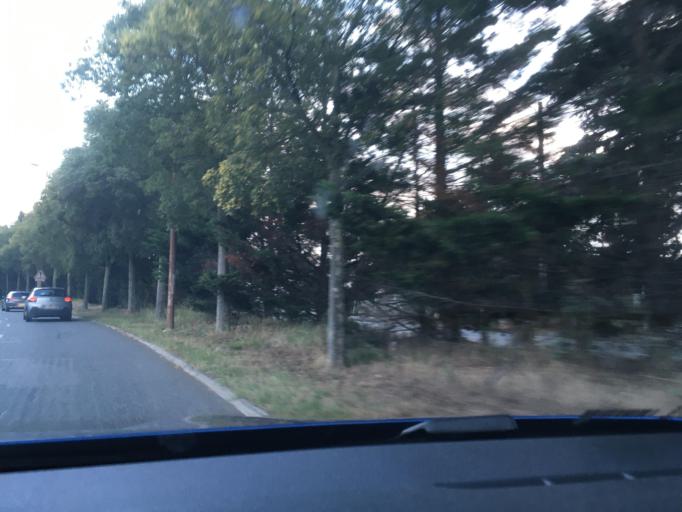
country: FR
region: Midi-Pyrenees
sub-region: Departement de la Haute-Garonne
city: Blagnac
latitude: 43.5832
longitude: 1.3980
